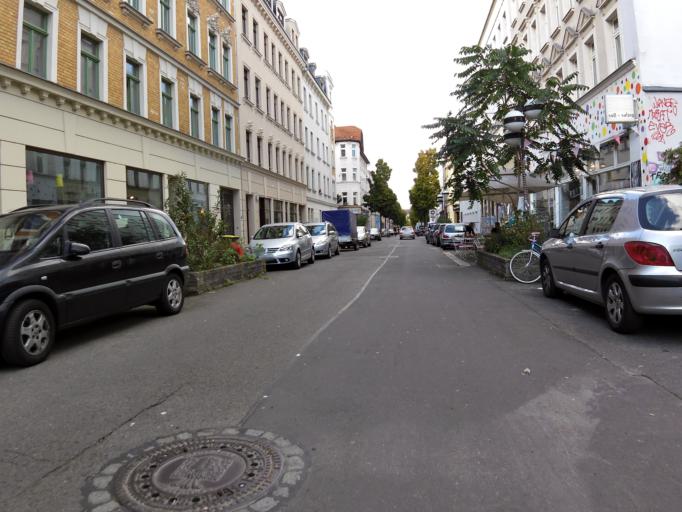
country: DE
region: Saxony
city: Leipzig
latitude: 51.3321
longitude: 12.3328
